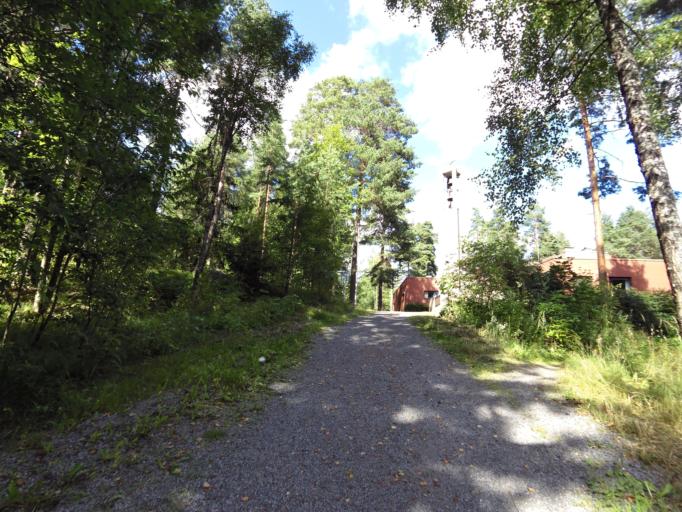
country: FI
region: Pirkanmaa
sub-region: Tampere
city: Pirkkala
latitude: 61.5049
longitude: 23.6242
